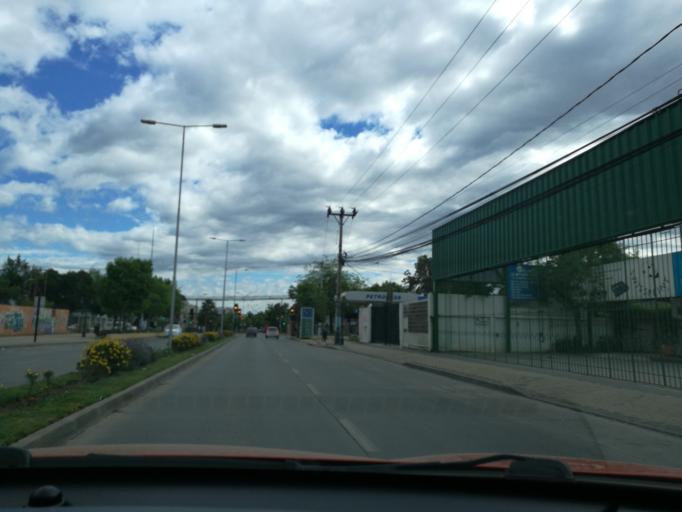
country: CL
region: O'Higgins
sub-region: Provincia de Cachapoal
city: Rancagua
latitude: -34.1675
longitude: -70.7345
